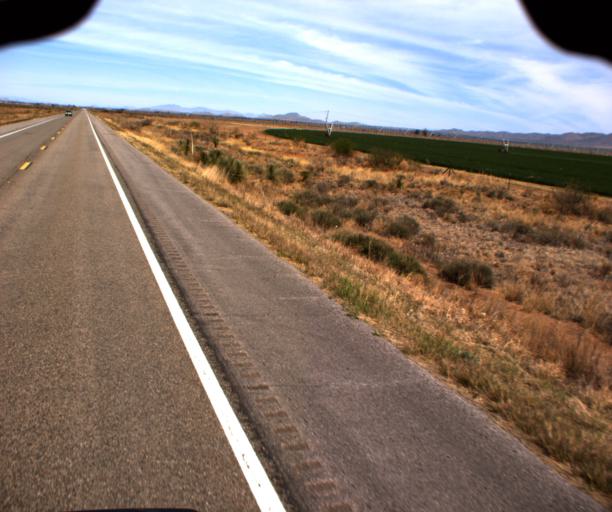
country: US
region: Arizona
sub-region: Cochise County
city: Pirtleville
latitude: 31.6088
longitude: -109.6704
